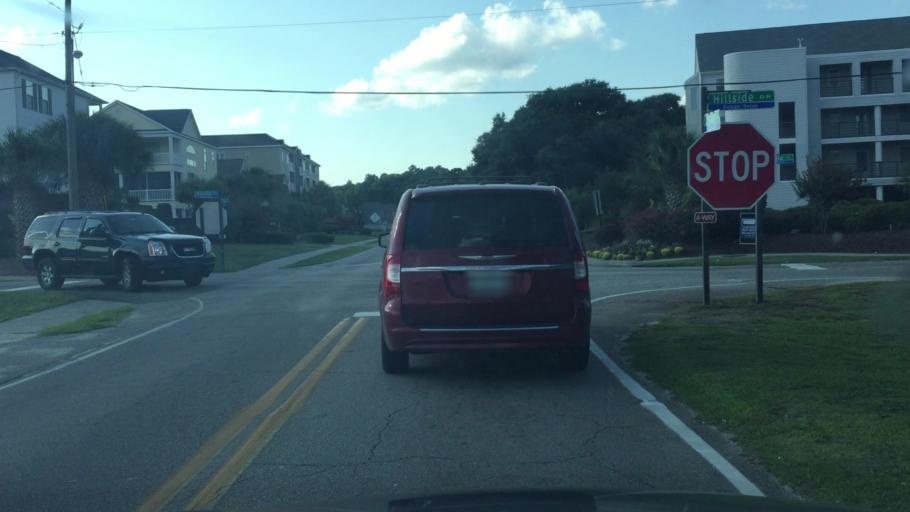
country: US
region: South Carolina
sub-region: Horry County
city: North Myrtle Beach
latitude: 33.8210
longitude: -78.6709
